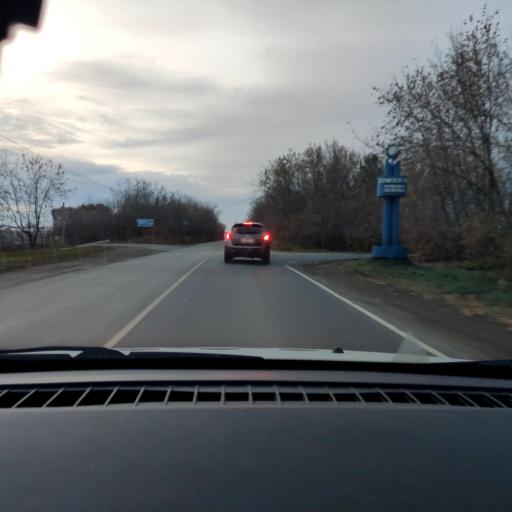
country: RU
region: Perm
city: Gamovo
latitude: 57.9054
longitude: 56.1694
